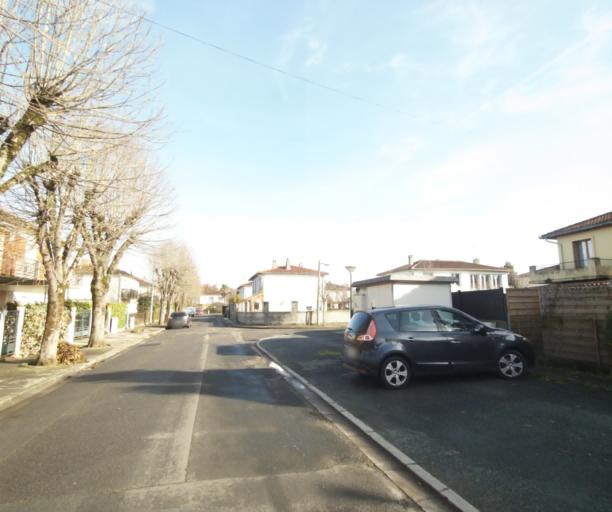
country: FR
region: Midi-Pyrenees
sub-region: Departement de la Haute-Garonne
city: Villemur-sur-Tarn
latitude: 43.8646
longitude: 1.4947
